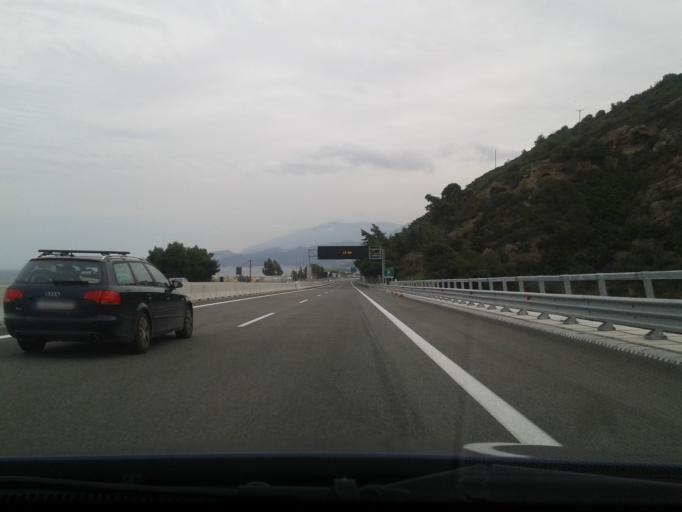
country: GR
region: West Greece
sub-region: Nomos Achaias
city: Siliveniotika
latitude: 38.1670
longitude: 22.3280
